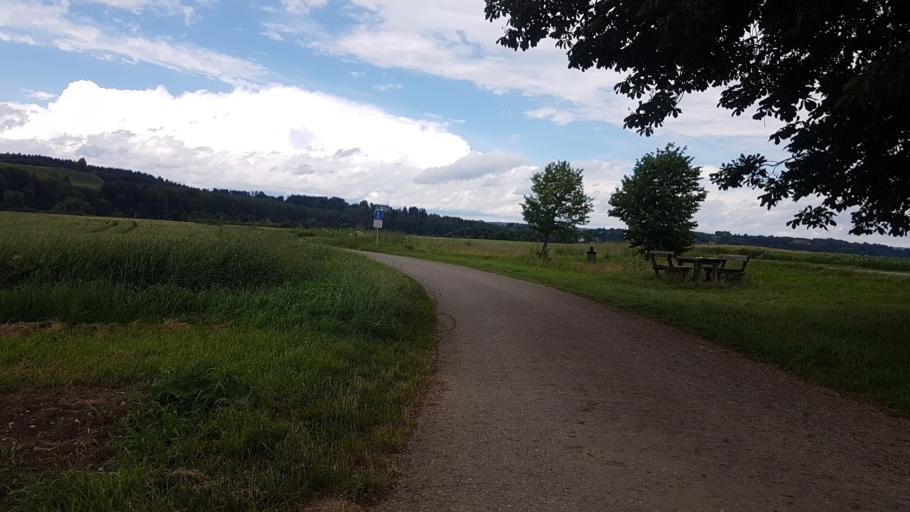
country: DE
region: Baden-Wuerttemberg
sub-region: Tuebingen Region
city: Herbertingen
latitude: 48.0904
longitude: 9.4233
